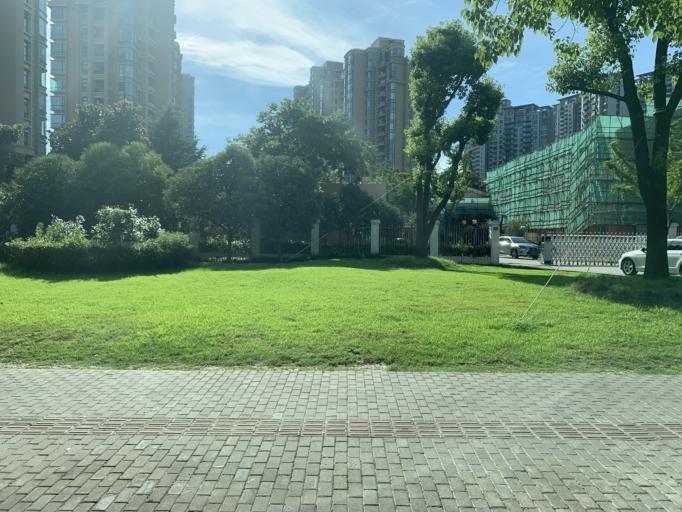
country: CN
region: Shanghai Shi
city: Huamu
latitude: 31.2086
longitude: 121.5320
